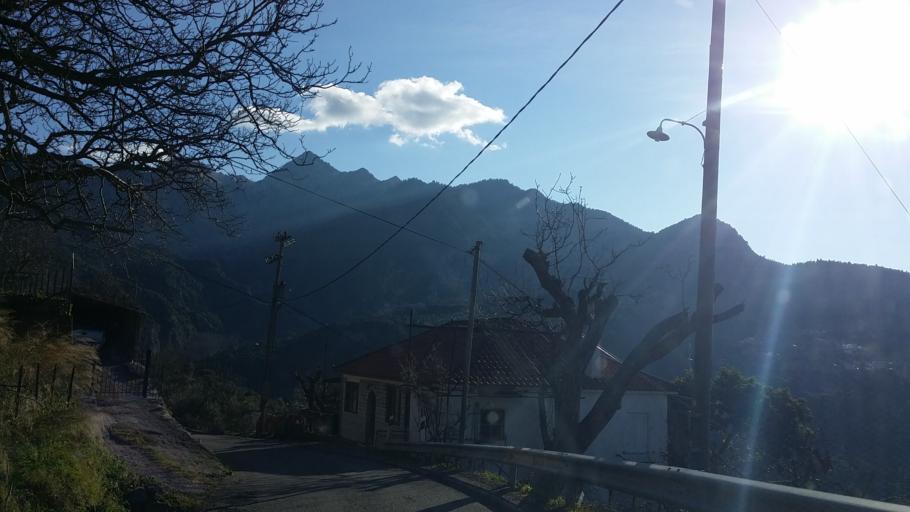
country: GR
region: Central Greece
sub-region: Nomos Evrytanias
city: Kerasochori
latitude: 38.8495
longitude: 21.5450
